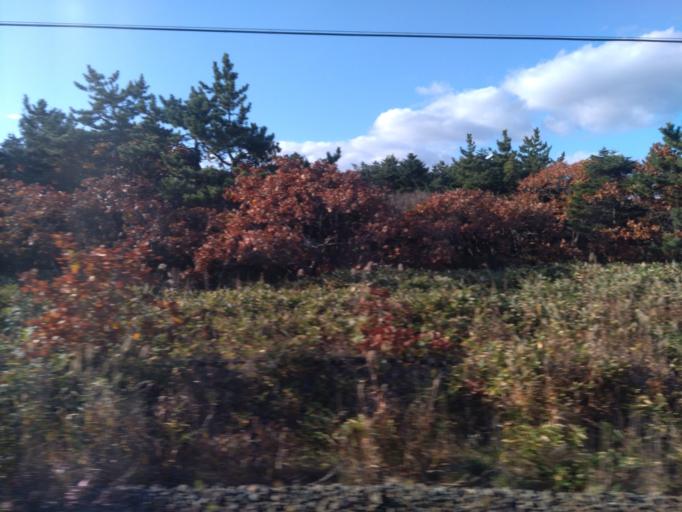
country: JP
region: Hokkaido
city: Niseko Town
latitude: 42.5659
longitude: 140.4361
